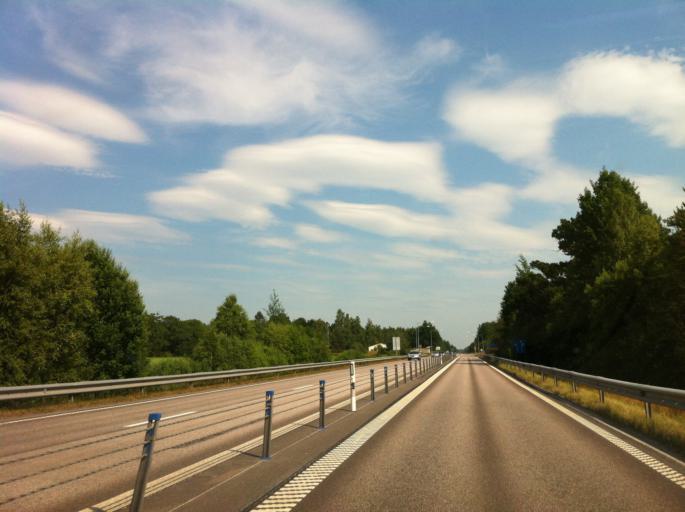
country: SE
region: Kalmar
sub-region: Kalmar Kommun
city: Trekanten
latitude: 56.7193
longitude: 16.0342
